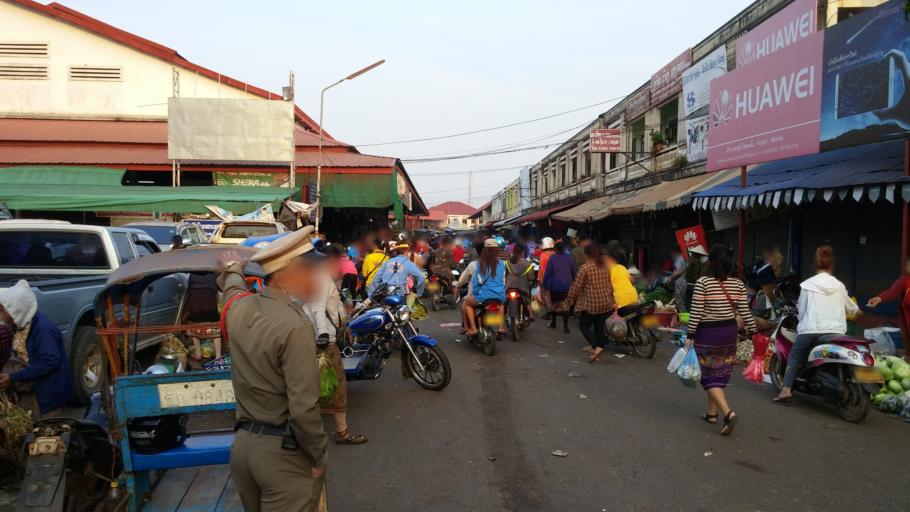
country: LA
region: Champasak
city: Pakxe
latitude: 15.1170
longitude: 105.8149
